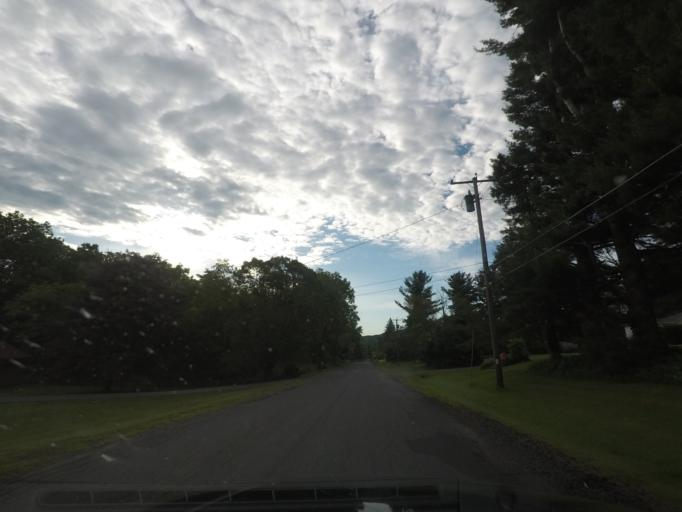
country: US
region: New York
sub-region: Dutchess County
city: Pine Plains
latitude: 41.9612
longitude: -73.5070
